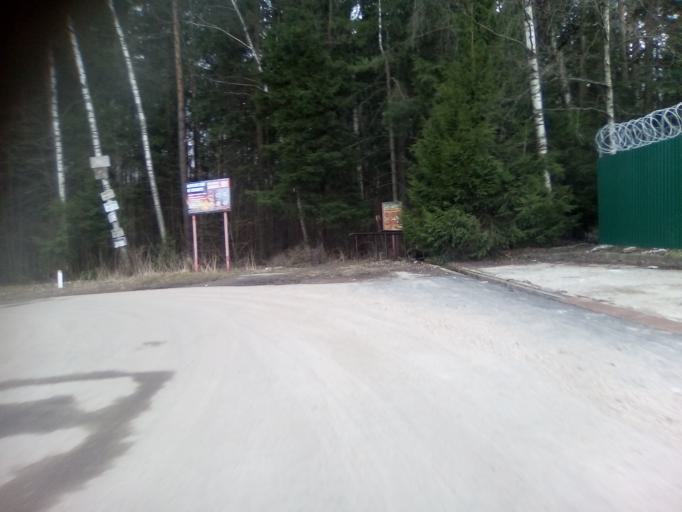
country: RU
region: Moskovskaya
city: Moskovskiy
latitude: 55.5850
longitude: 37.3276
